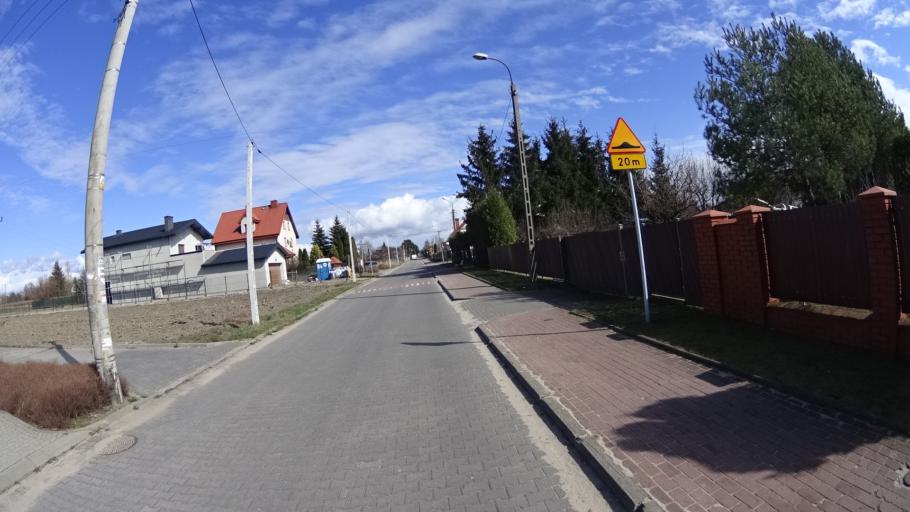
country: PL
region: Masovian Voivodeship
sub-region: Powiat warszawski zachodni
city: Jozefow
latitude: 52.2037
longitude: 20.7044
